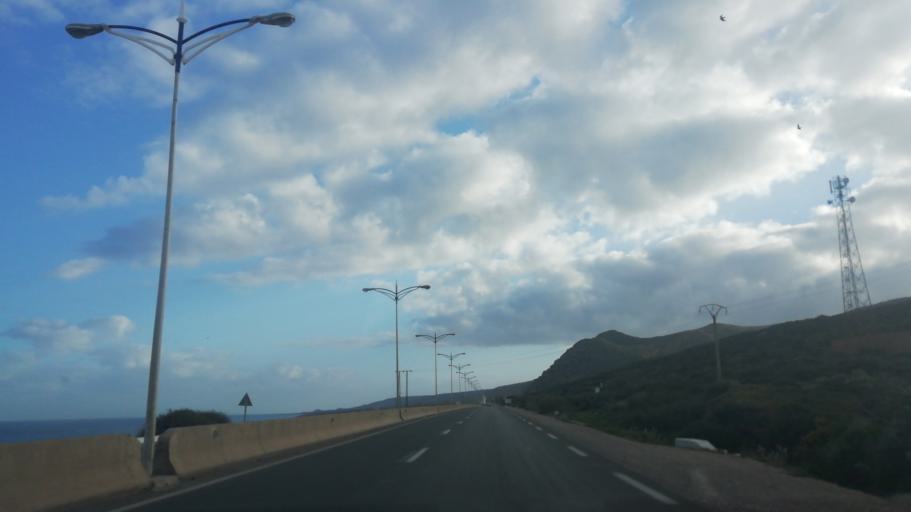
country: DZ
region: Mostaganem
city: Mostaganem
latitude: 36.0493
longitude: 0.1491
